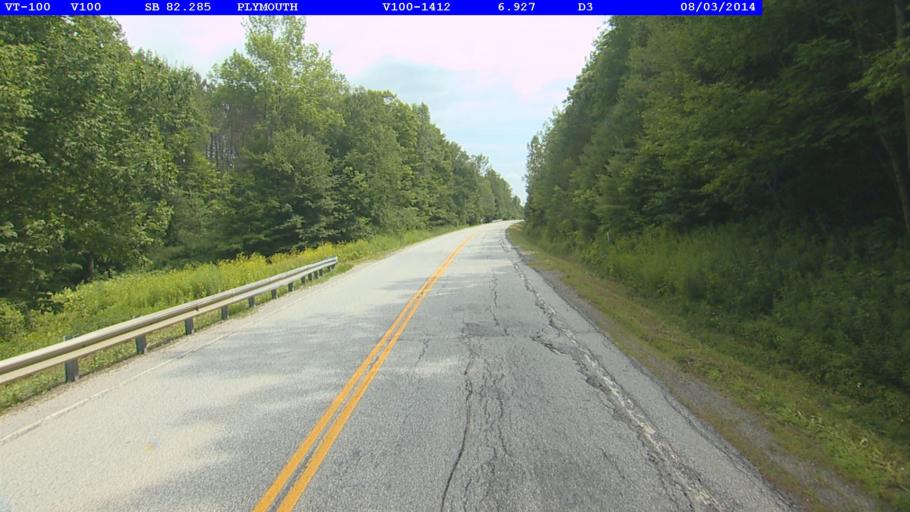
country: US
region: Vermont
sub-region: Rutland County
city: Rutland
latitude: 43.5502
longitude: -72.7539
